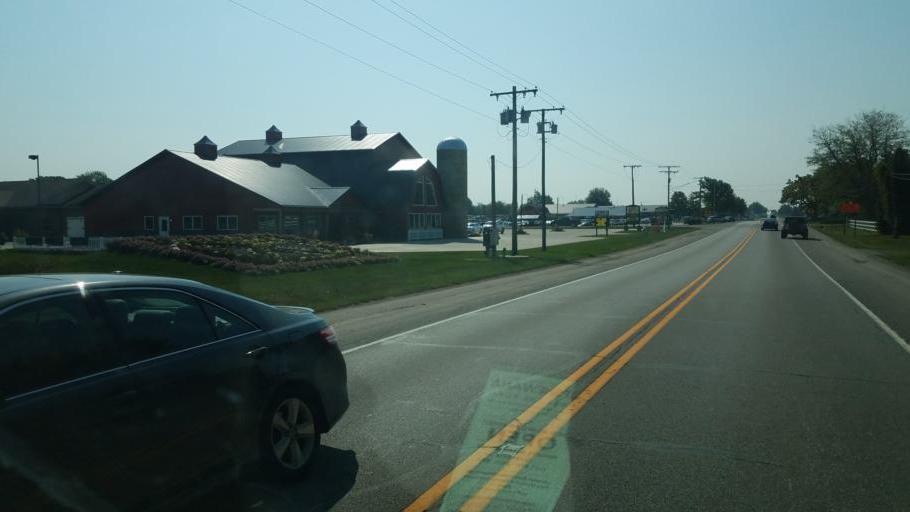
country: US
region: Indiana
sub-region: Elkhart County
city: Middlebury
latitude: 41.6602
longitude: -85.5804
